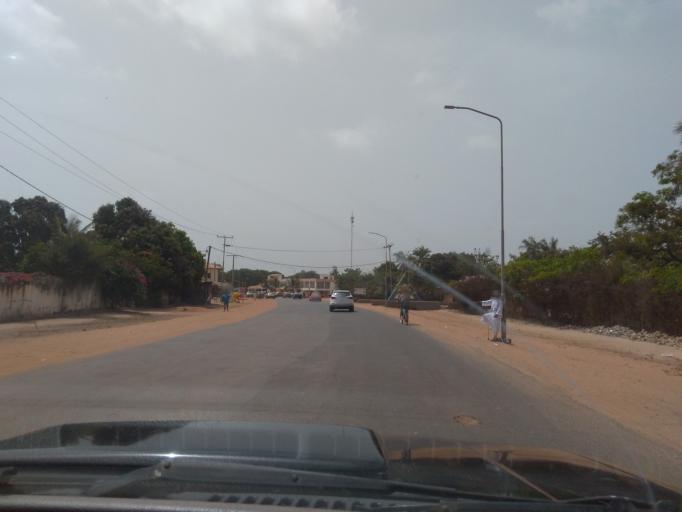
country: GM
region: Western
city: Sukuta
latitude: 13.4385
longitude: -16.7016
